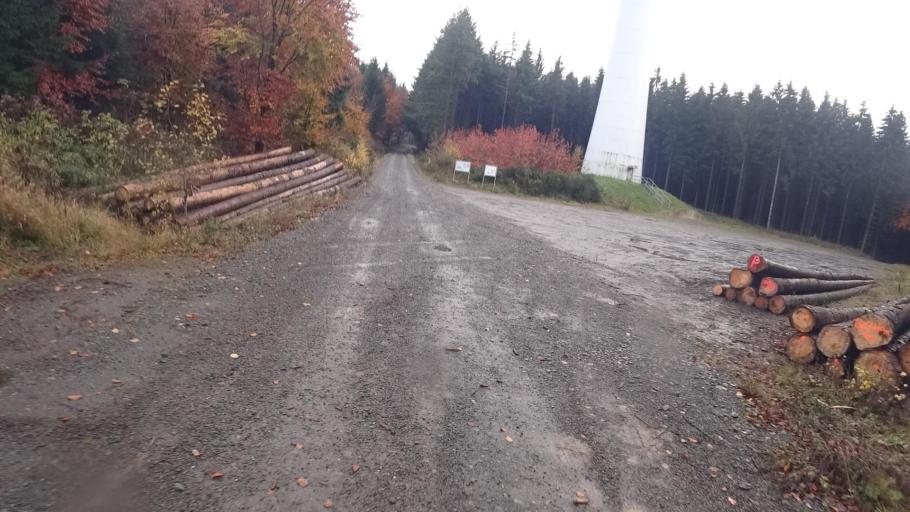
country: DE
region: Rheinland-Pfalz
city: Braunshorn
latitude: 50.1049
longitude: 7.5056
